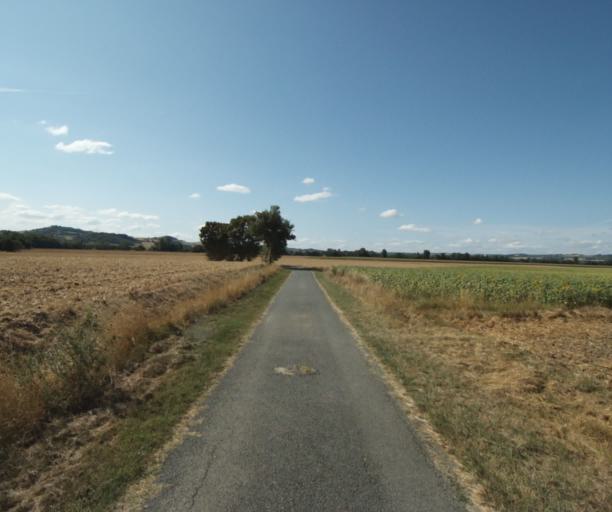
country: FR
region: Midi-Pyrenees
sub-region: Departement de la Haute-Garonne
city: Revel
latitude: 43.5051
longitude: 1.9736
